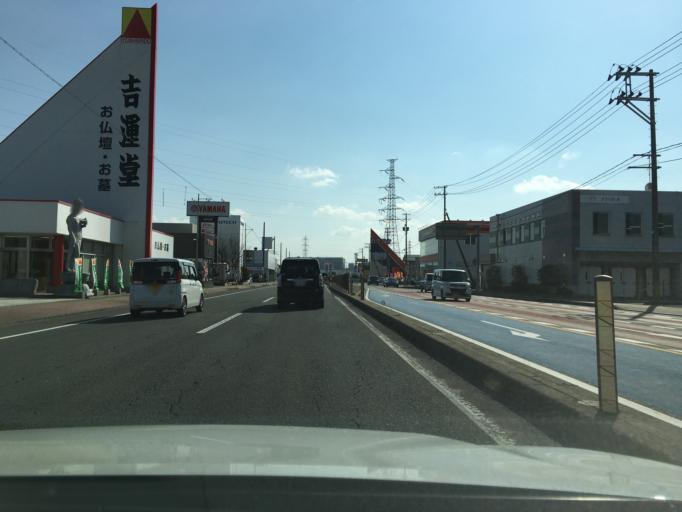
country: JP
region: Yamagata
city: Sakata
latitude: 38.9007
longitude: 139.8561
